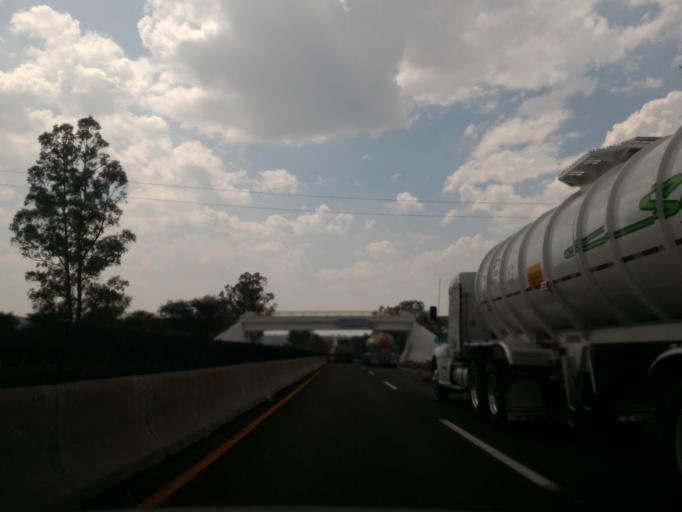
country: MX
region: Jalisco
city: Encarnacion de Diaz
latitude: 21.4540
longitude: -102.2047
